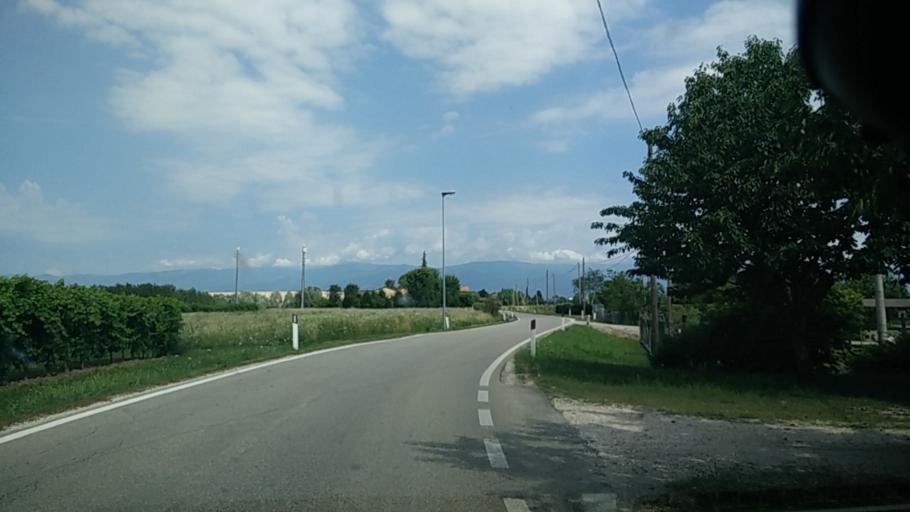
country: IT
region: Veneto
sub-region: Provincia di Treviso
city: Portobuffole
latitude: 45.8539
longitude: 12.5479
